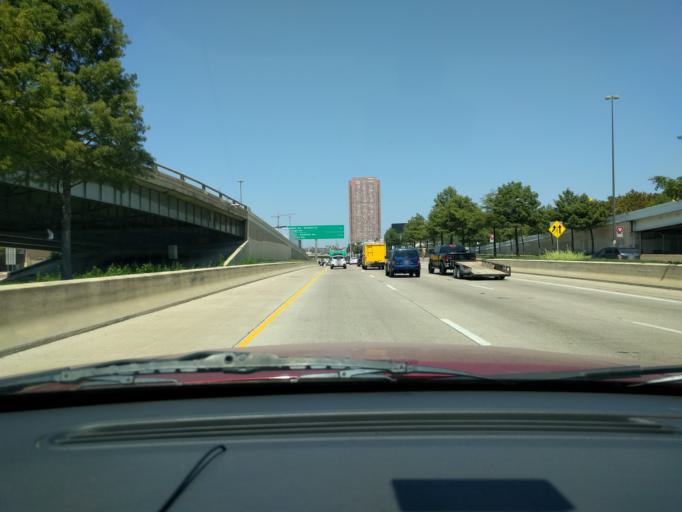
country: US
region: Texas
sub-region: Dallas County
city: Dallas
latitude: 32.7955
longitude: -96.7927
